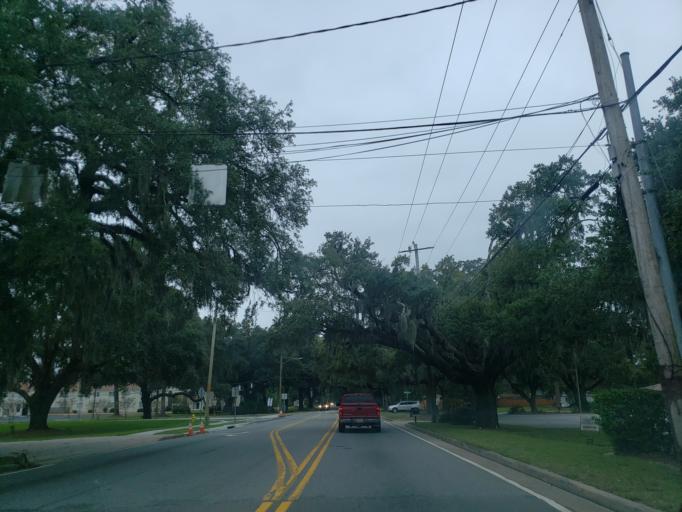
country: US
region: Georgia
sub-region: Chatham County
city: Thunderbolt
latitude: 32.0190
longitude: -81.0753
